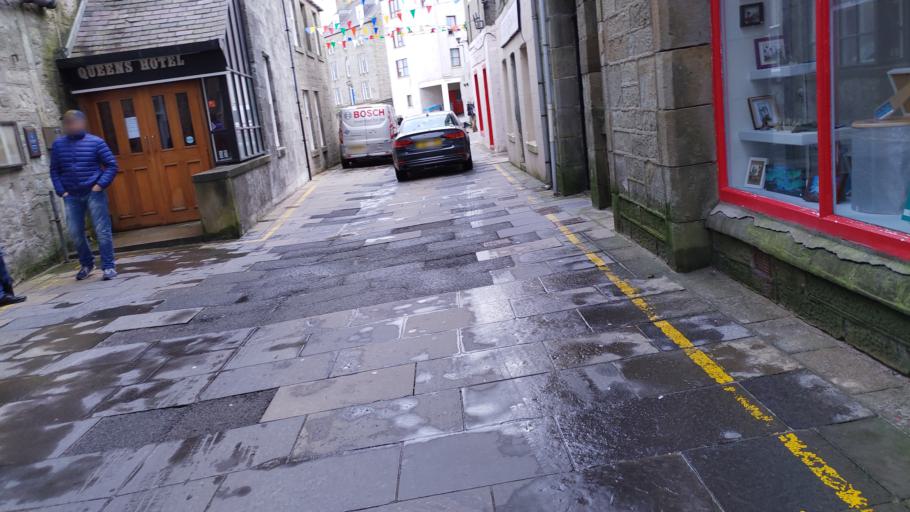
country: GB
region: Scotland
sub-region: Shetland Islands
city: Shetland
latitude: 60.1531
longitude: -1.1403
